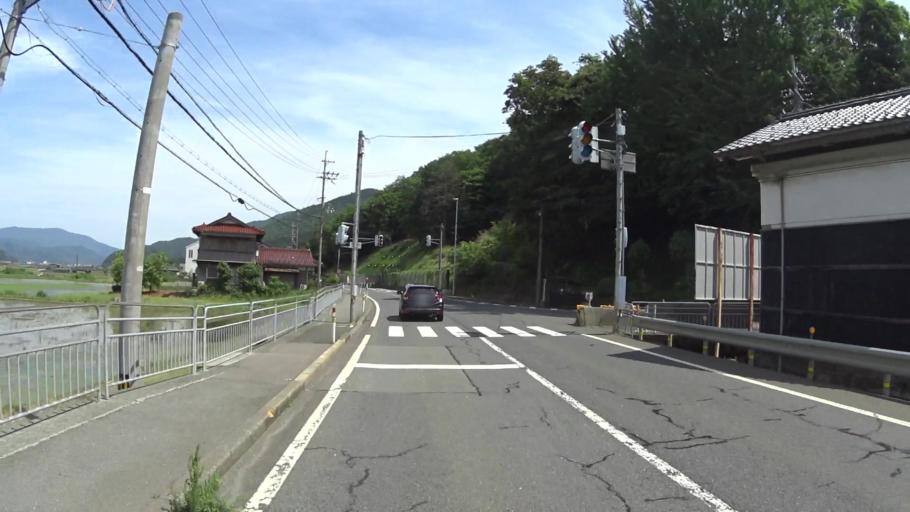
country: JP
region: Fukui
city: Obama
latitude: 35.4773
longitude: 135.7987
